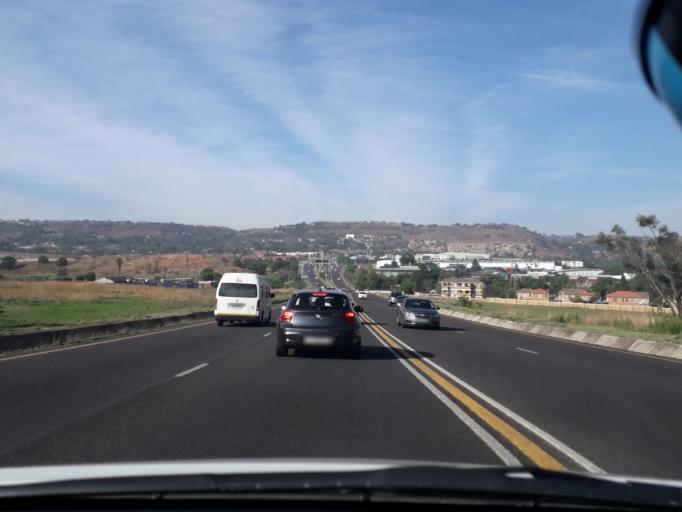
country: ZA
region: Gauteng
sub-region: City of Johannesburg Metropolitan Municipality
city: Roodepoort
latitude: -26.1188
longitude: 27.9144
